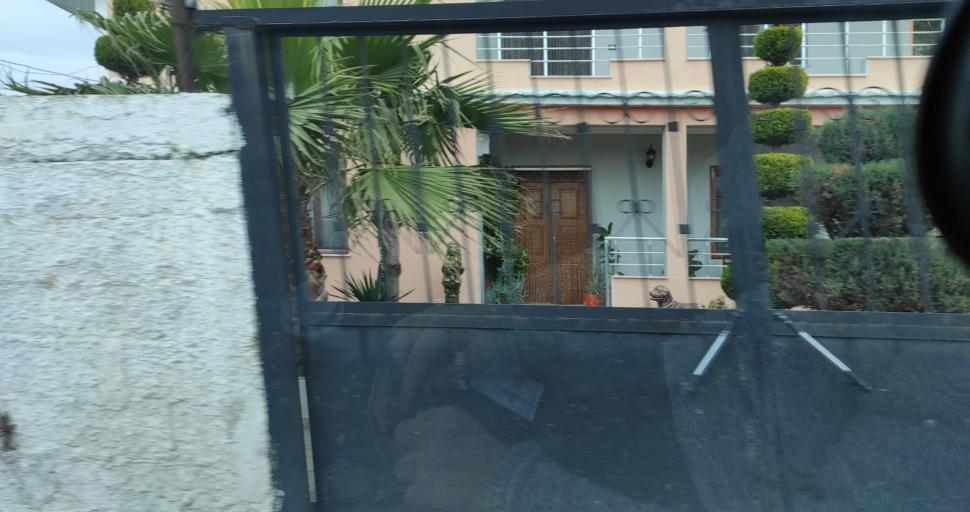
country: AL
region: Lezhe
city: Lezhe
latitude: 41.7835
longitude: 19.6296
